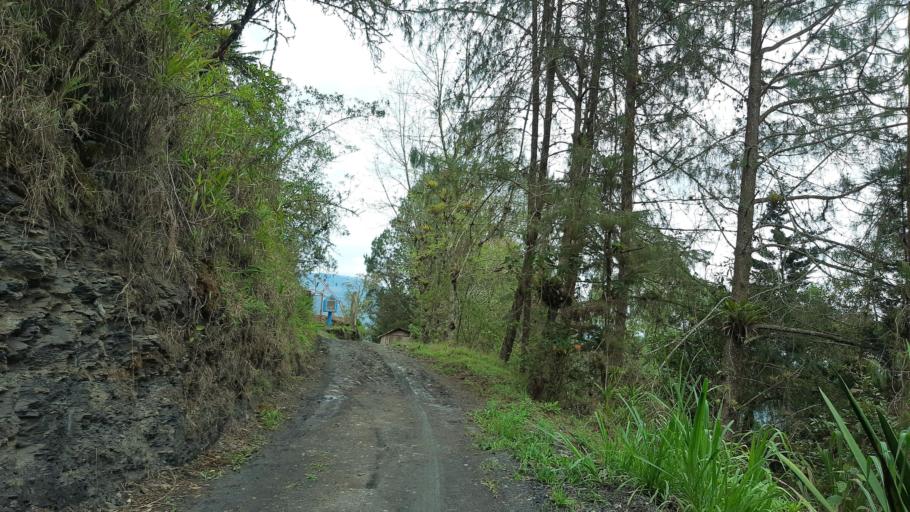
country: CO
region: Boyaca
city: Garagoa
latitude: 5.0516
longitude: -73.3465
